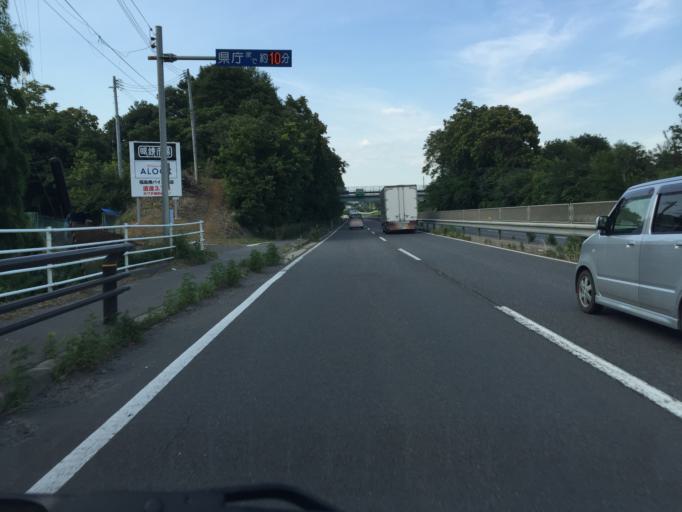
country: JP
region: Fukushima
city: Fukushima-shi
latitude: 37.7010
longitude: 140.4605
